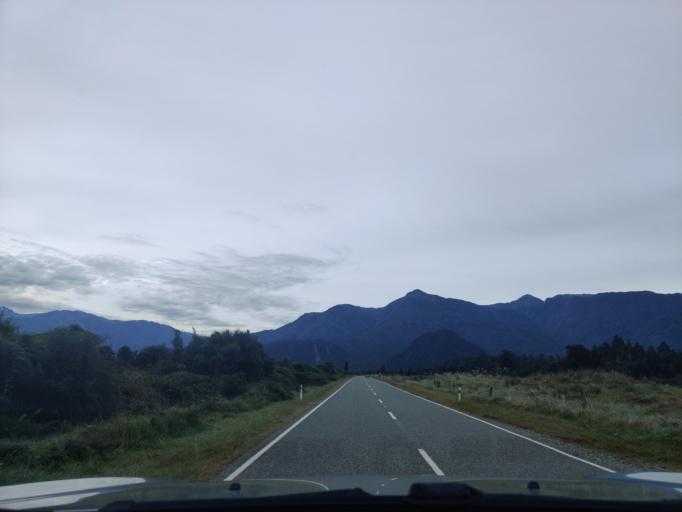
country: NZ
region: West Coast
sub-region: Westland District
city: Hokitika
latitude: -43.2637
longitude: 170.2898
